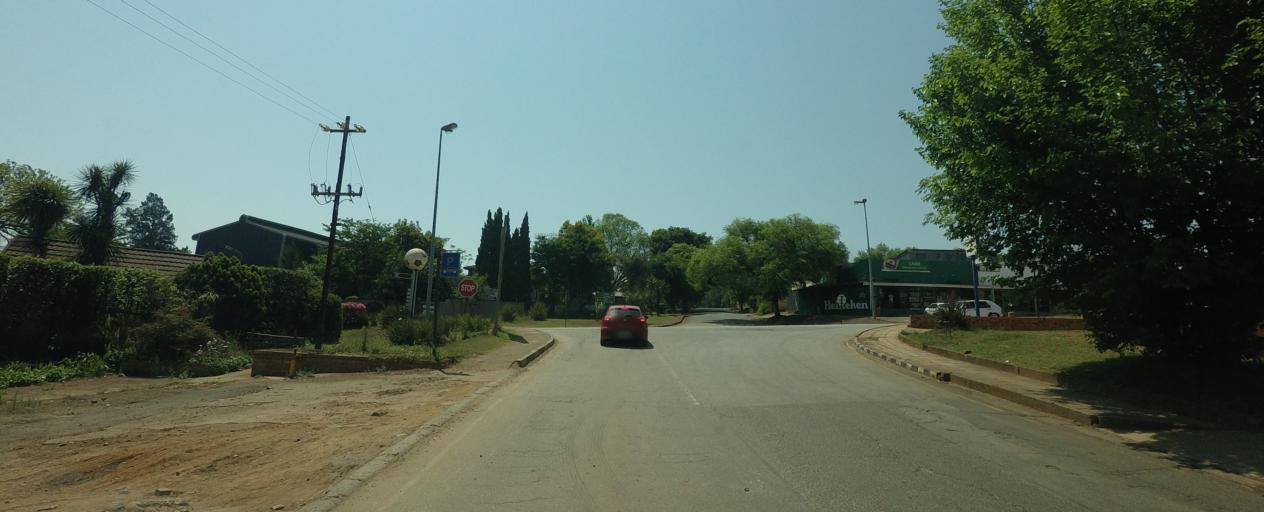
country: ZA
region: Mpumalanga
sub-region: Ehlanzeni District
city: Graksop
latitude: -25.0911
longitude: 30.7782
